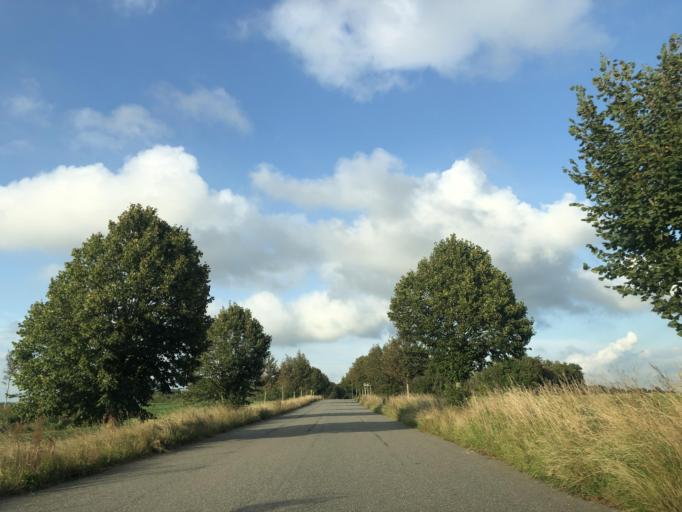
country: DK
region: North Denmark
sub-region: Vesthimmerland Kommune
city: Aars
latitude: 56.7824
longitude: 9.5850
